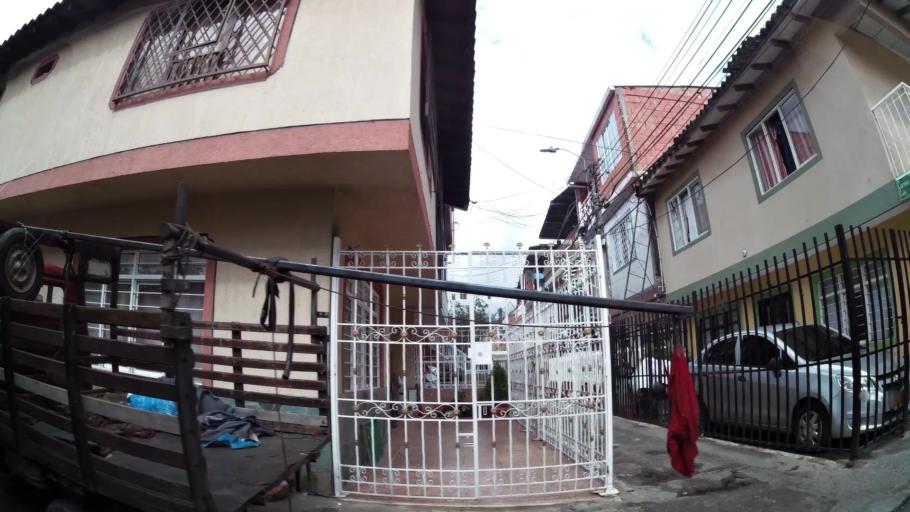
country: CO
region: Valle del Cauca
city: Cali
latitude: 3.3885
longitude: -76.5502
